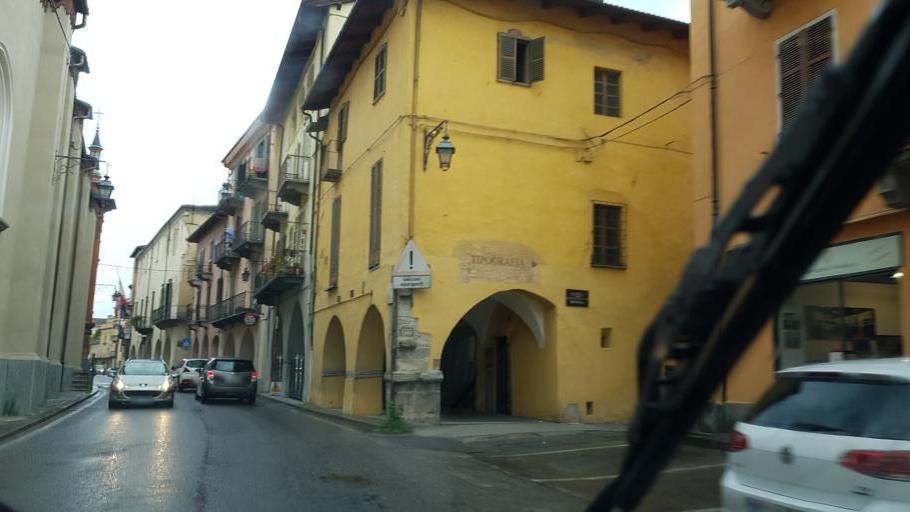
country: IT
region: Piedmont
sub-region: Provincia di Cuneo
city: Dronero
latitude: 44.4672
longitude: 7.3639
